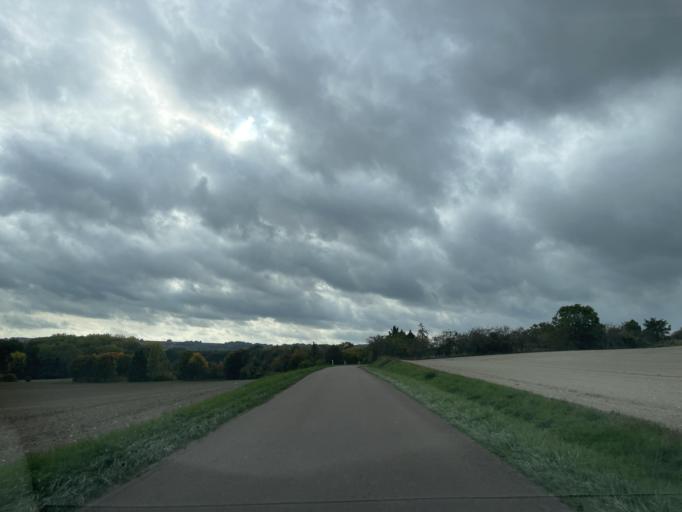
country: FR
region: Bourgogne
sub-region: Departement de l'Yonne
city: Aillant-sur-Tholon
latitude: 47.8290
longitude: 3.3445
